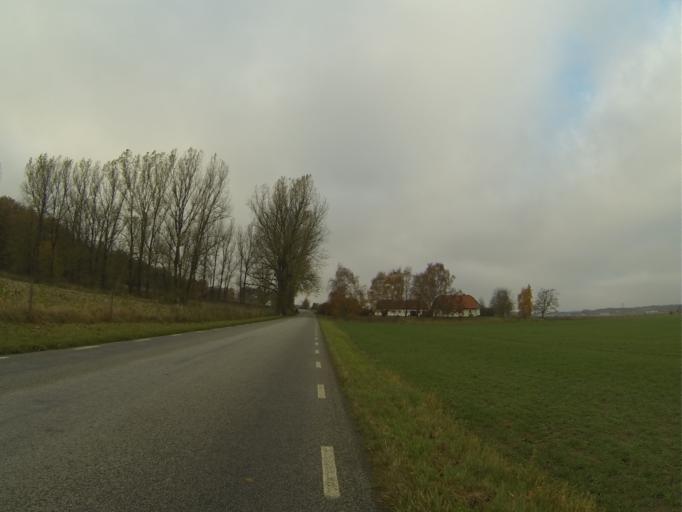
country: SE
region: Skane
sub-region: Lunds Kommun
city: Genarp
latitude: 55.7085
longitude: 13.3739
